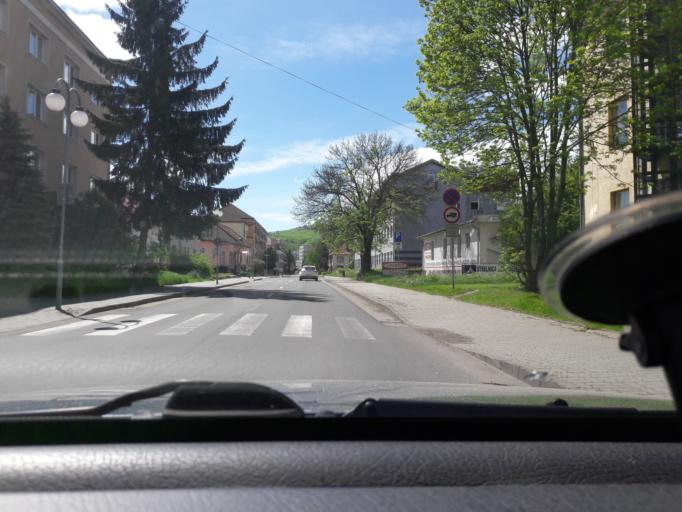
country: SK
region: Banskobystricky
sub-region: Okres Banska Bystrica
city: Zvolen
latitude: 48.5804
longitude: 19.1229
